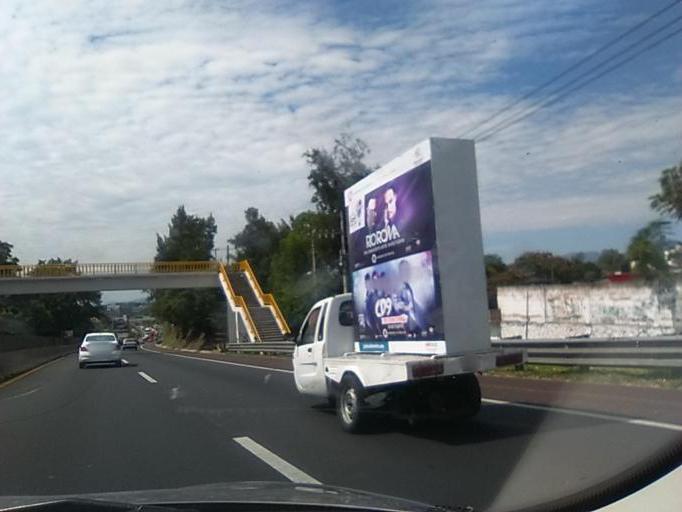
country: MX
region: Morelos
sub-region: Cuernavaca
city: Cuernavaca
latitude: 18.9095
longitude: -99.2093
